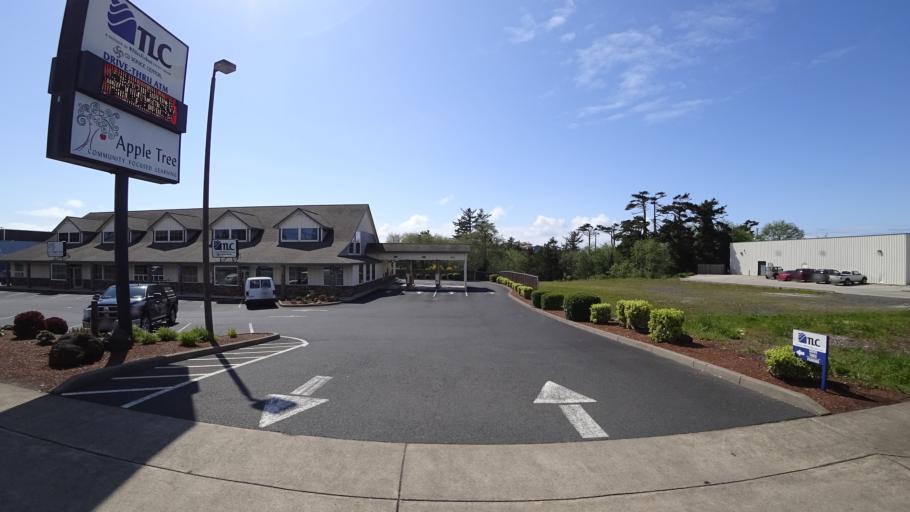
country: US
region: Oregon
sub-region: Lincoln County
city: Newport
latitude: 44.6498
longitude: -124.0531
